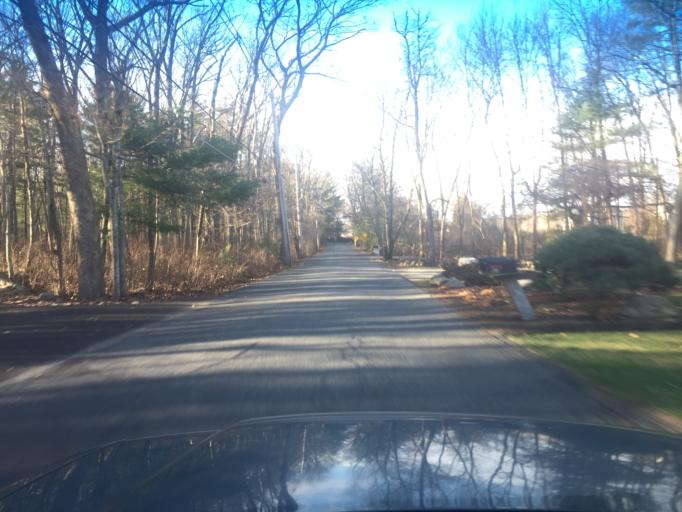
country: US
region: Massachusetts
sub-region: Middlesex County
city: Ashland
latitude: 42.2296
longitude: -71.4830
